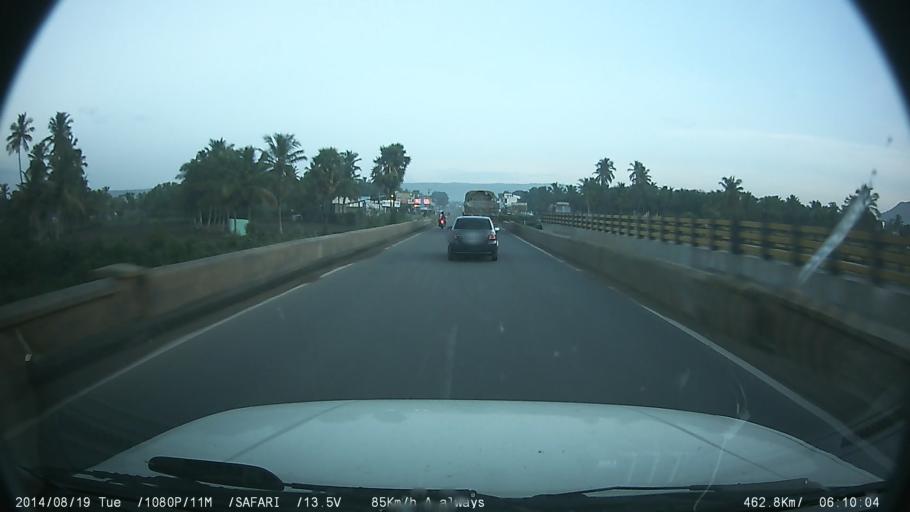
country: IN
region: Tamil Nadu
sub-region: Salem
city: Omalur
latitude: 11.9380
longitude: 78.0528
